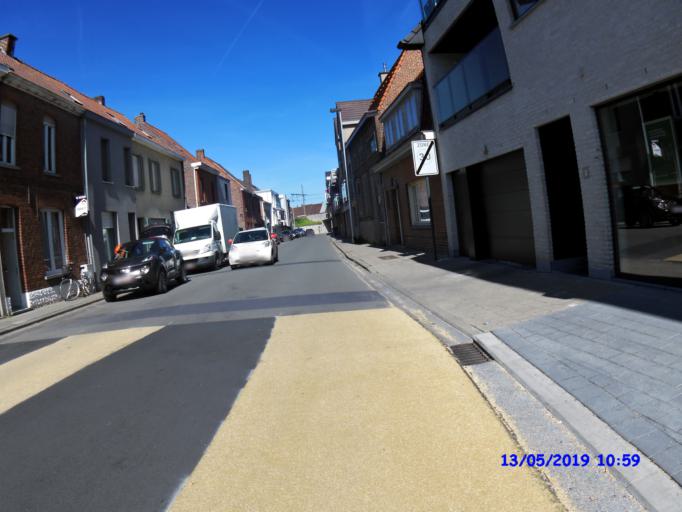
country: BE
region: Flanders
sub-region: Provincie West-Vlaanderen
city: Waregem
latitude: 50.8887
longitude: 3.4220
